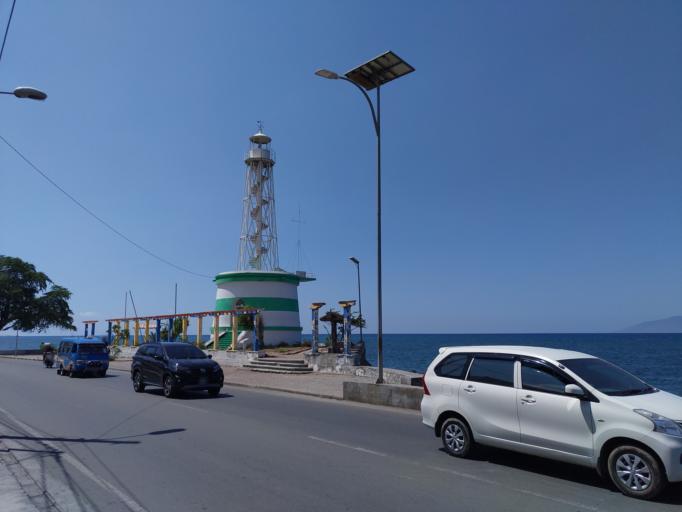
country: TL
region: Dili
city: Dili
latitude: -8.5486
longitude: 125.5691
